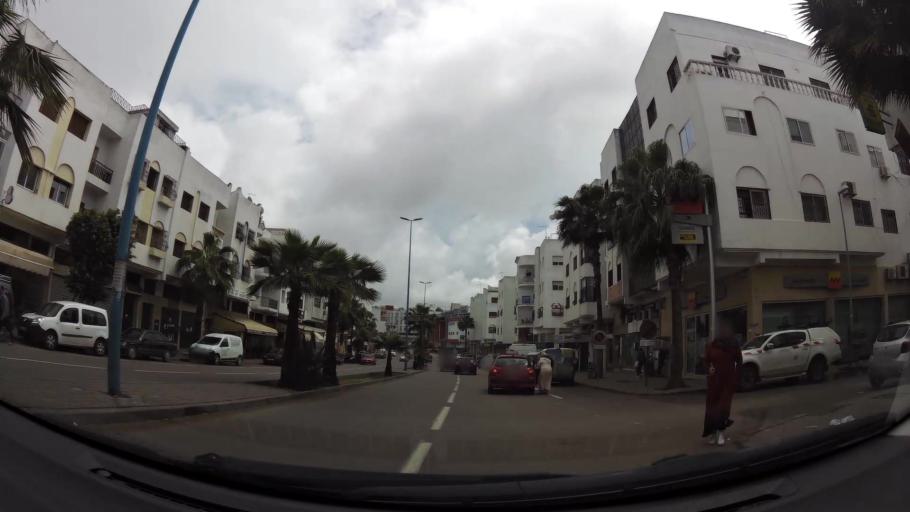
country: MA
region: Grand Casablanca
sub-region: Casablanca
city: Casablanca
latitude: 33.5404
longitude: -7.6828
